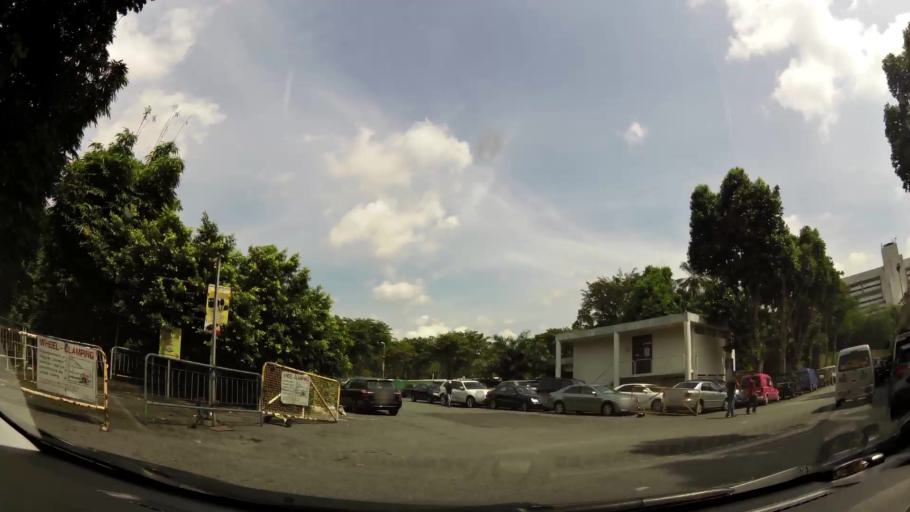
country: SG
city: Singapore
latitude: 1.3384
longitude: 103.7915
